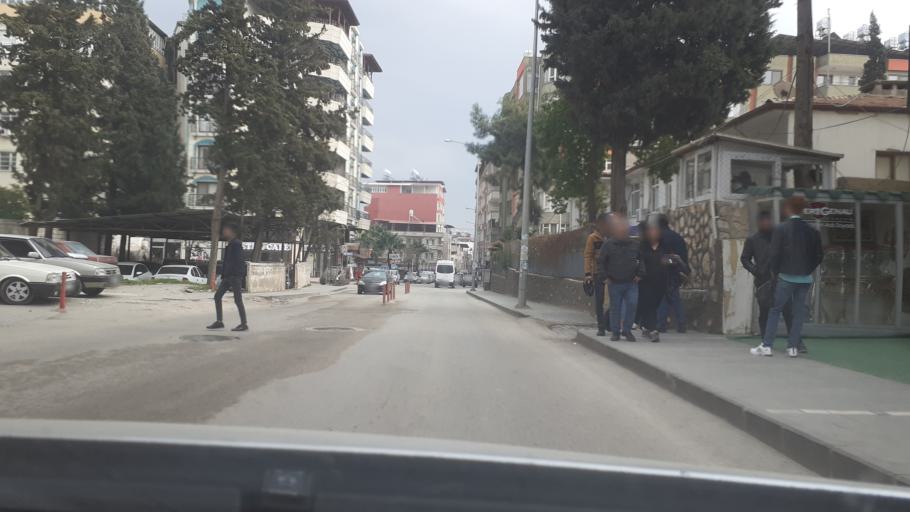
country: TR
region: Hatay
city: Kirikhan
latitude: 36.4980
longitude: 36.3533
